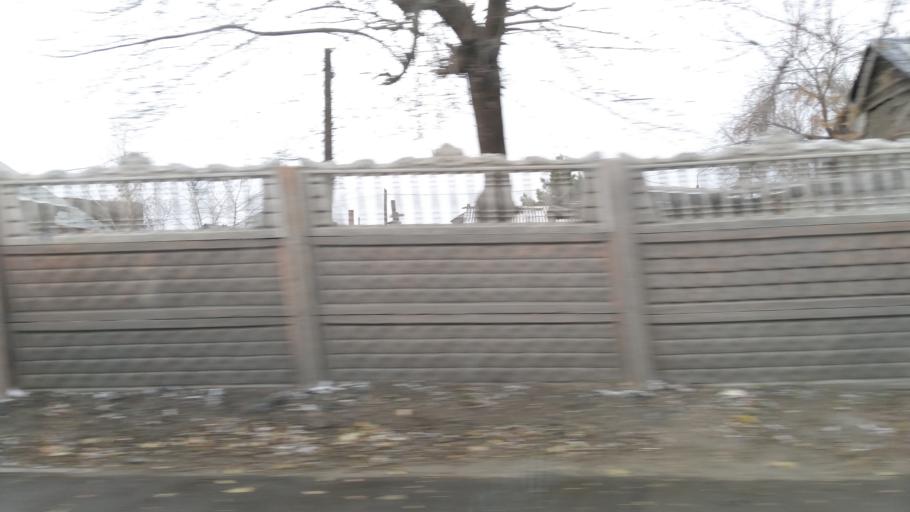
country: KZ
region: Pavlodar
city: Pavlodar
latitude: 52.2755
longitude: 76.9556
